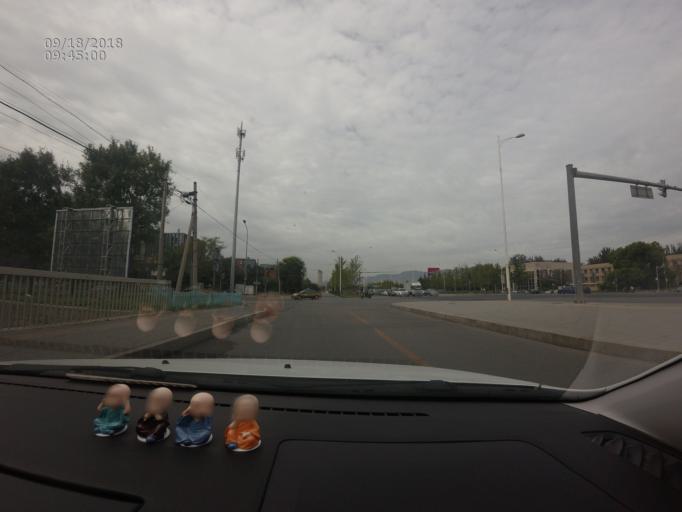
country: CN
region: Beijing
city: Xibeiwang
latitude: 40.0720
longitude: 116.2380
